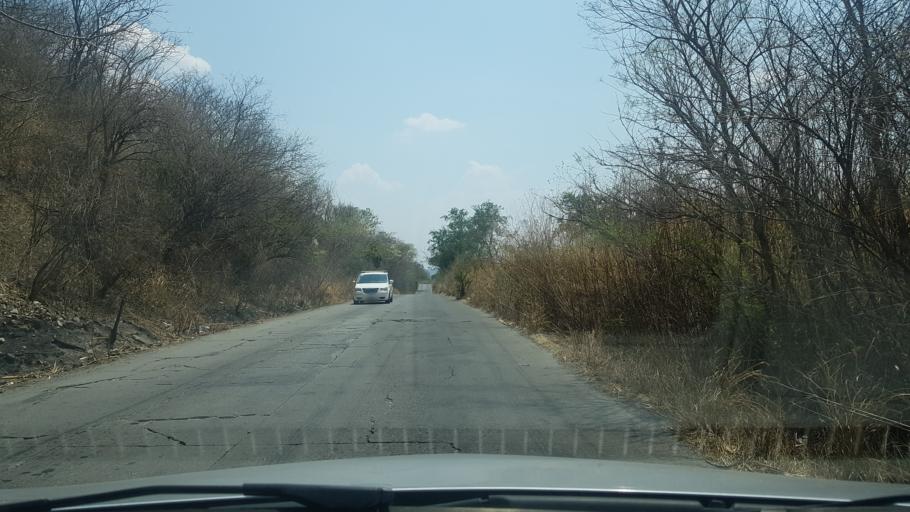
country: MX
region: Morelos
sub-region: Tlaltizapan de Zapata
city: Colonia Palo Prieto (Chipitongo)
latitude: 18.7823
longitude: -99.1046
